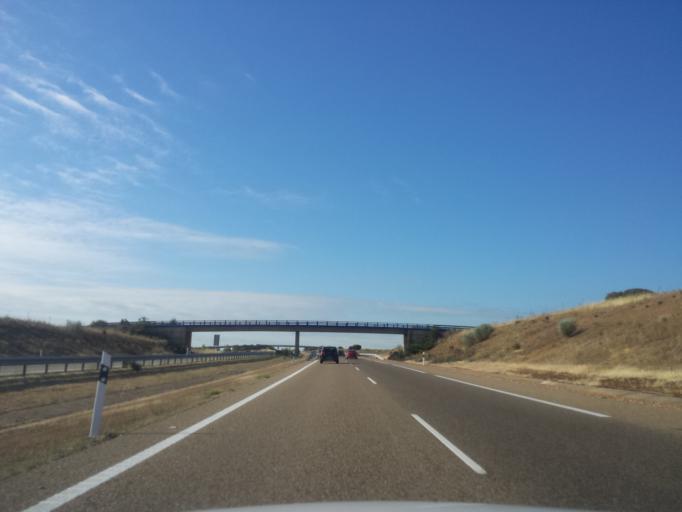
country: ES
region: Castille and Leon
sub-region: Provincia de Leon
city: Valdevimbre
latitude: 42.3920
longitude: -5.5961
